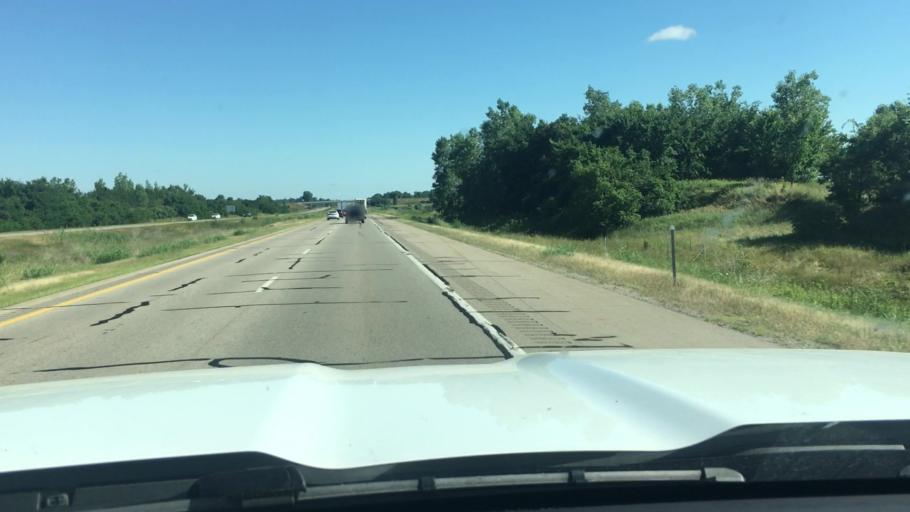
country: US
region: Michigan
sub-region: Clinton County
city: Saint Johns
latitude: 42.9482
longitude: -84.5184
